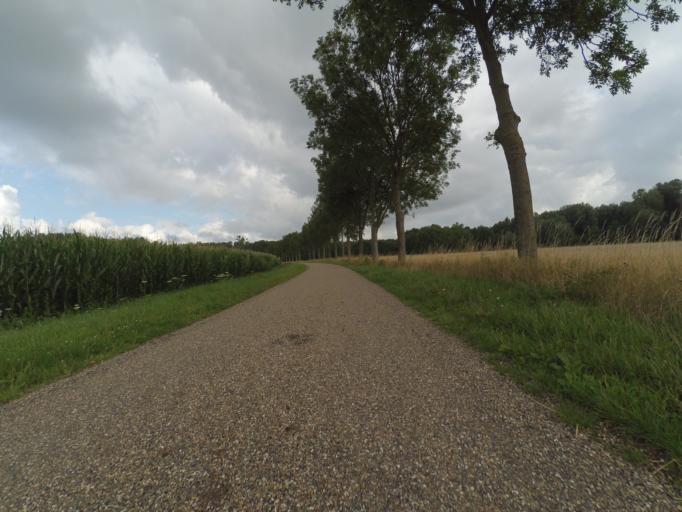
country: NL
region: Limburg
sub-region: Gemeente Sittard-Geleen
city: Limbricht
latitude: 51.0487
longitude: 5.8508
